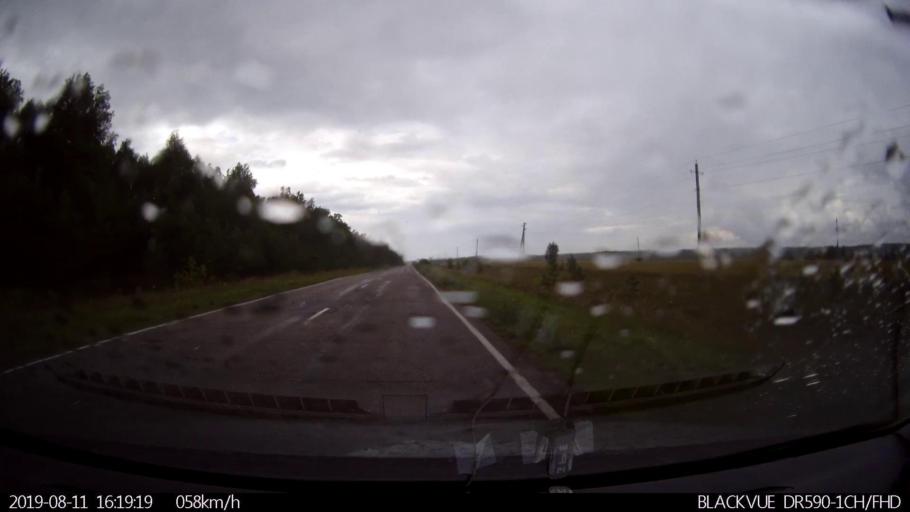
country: RU
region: Ulyanovsk
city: Mayna
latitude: 54.0627
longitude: 47.6080
